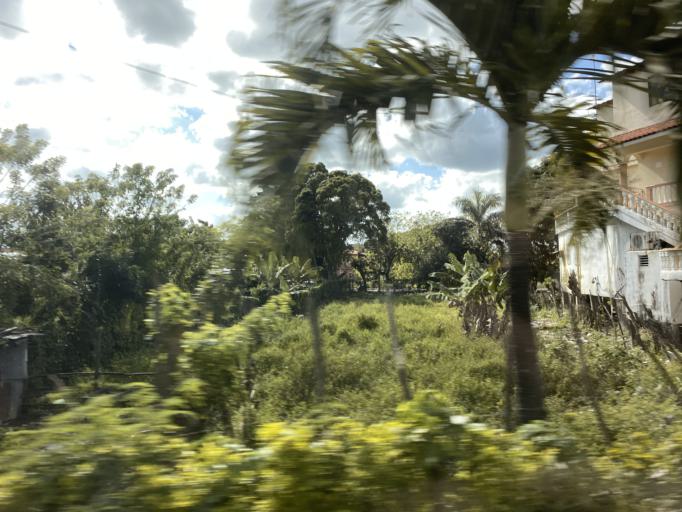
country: DO
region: Espaillat
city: Jamao al Norte
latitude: 19.6688
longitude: -70.3683
